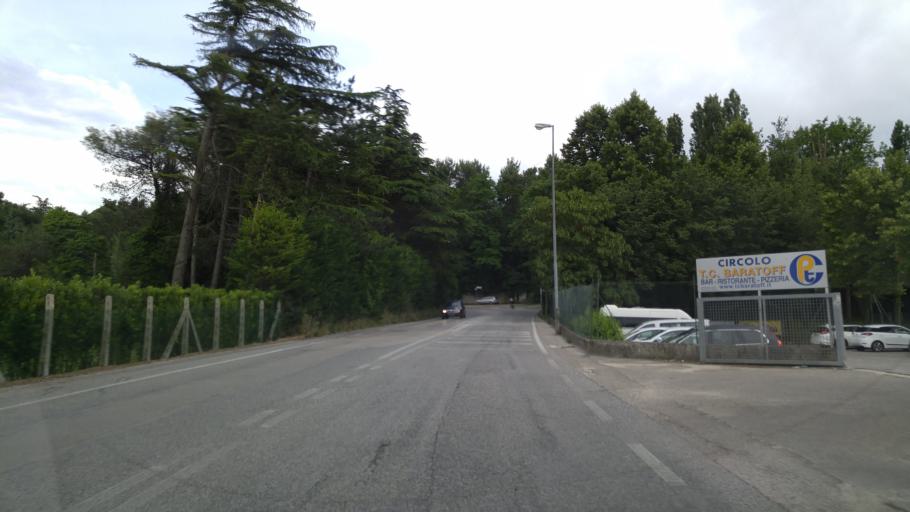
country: IT
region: The Marches
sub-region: Provincia di Pesaro e Urbino
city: Pesaro
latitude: 43.8893
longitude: 12.9129
